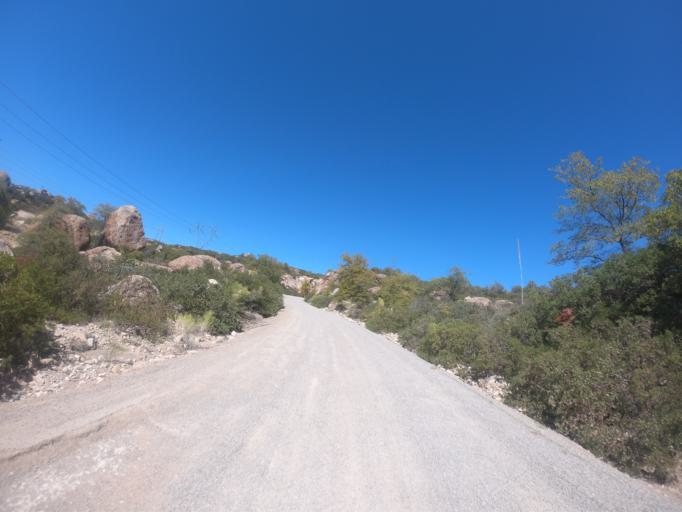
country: US
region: Arizona
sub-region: Pinal County
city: Superior
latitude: 33.3320
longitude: -111.0375
